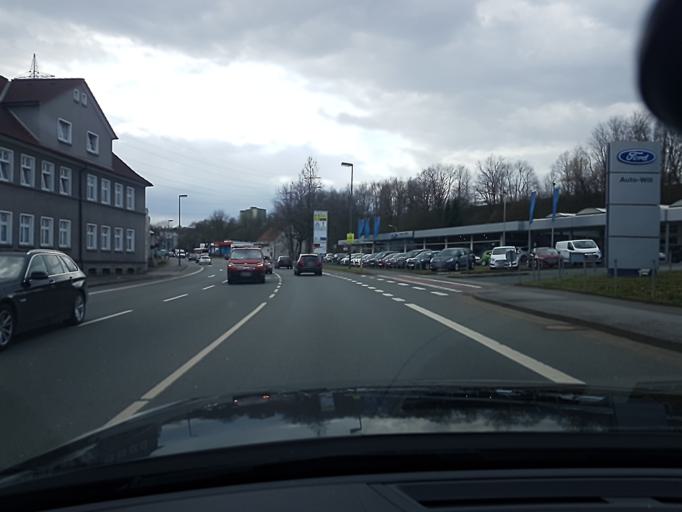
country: DE
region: North Rhine-Westphalia
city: Iserlohn
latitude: 51.3980
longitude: 7.6934
